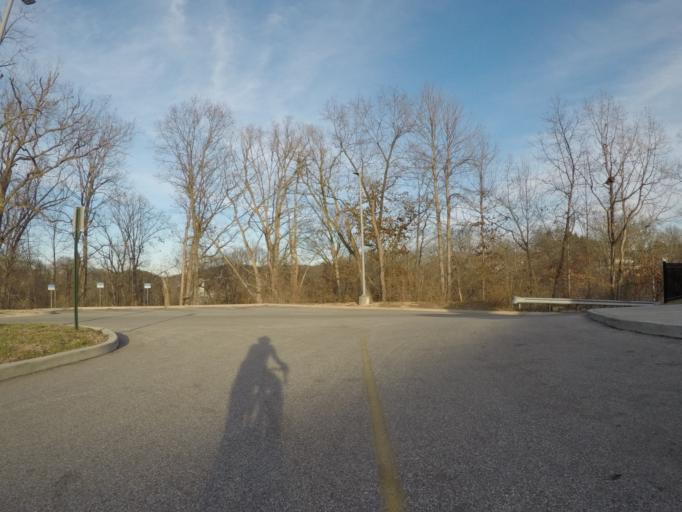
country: US
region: West Virginia
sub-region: Cabell County
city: Huntington
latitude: 38.4079
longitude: -82.3911
